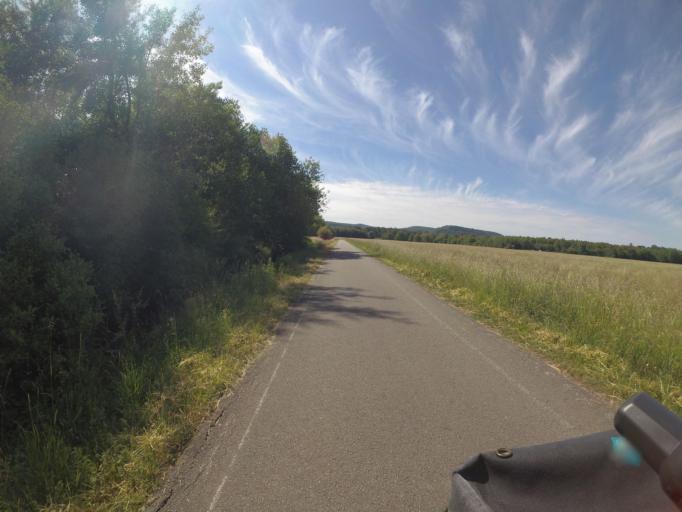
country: DE
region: Rheinland-Pfalz
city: Ramstein-Miesenbach
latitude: 49.4331
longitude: 7.5693
